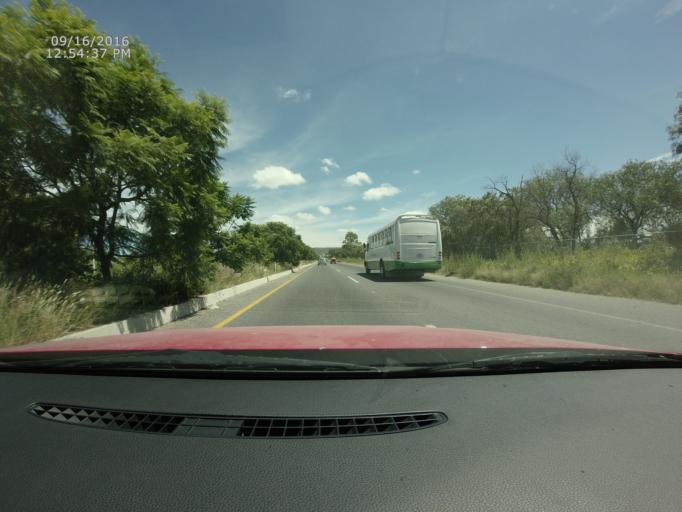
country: MX
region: Queretaro
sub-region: Colon
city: Purisima de Cubos (La Purisima)
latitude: 20.6334
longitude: -100.1169
